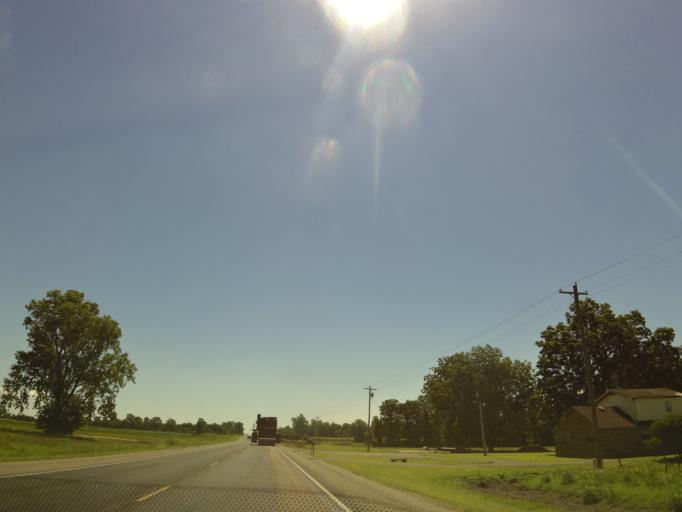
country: US
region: Missouri
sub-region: New Madrid County
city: Lilbourn
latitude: 36.5543
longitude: -89.7464
